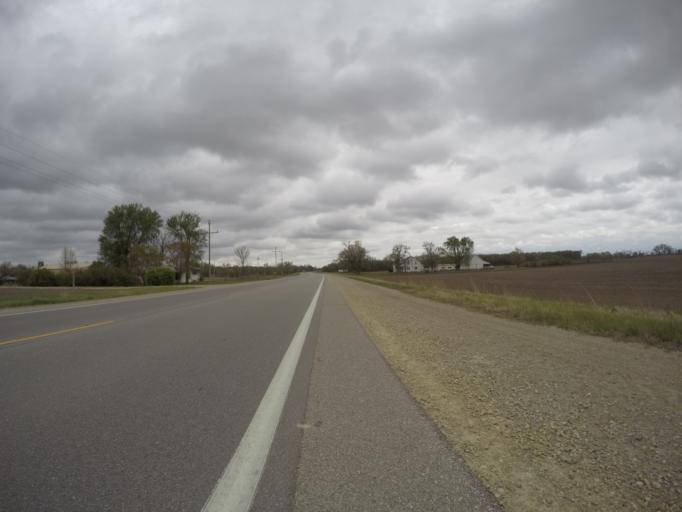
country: US
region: Kansas
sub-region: Pottawatomie County
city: Wamego
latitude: 39.1906
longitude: -96.3052
